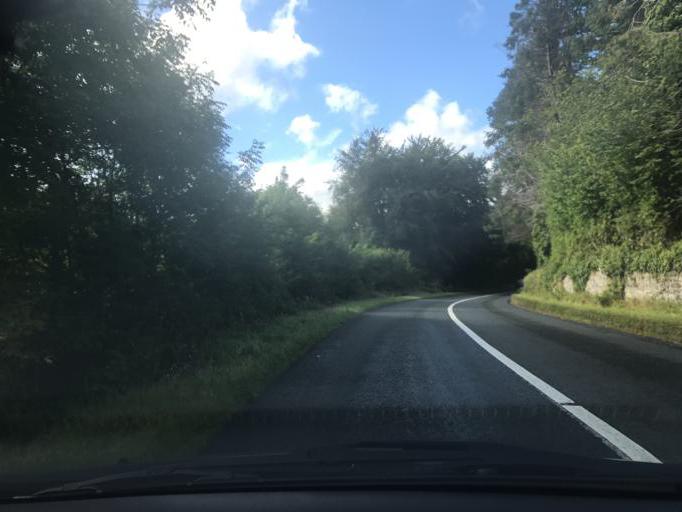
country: IE
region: Connaught
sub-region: Sligo
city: Collooney
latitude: 54.2027
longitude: -8.4621
